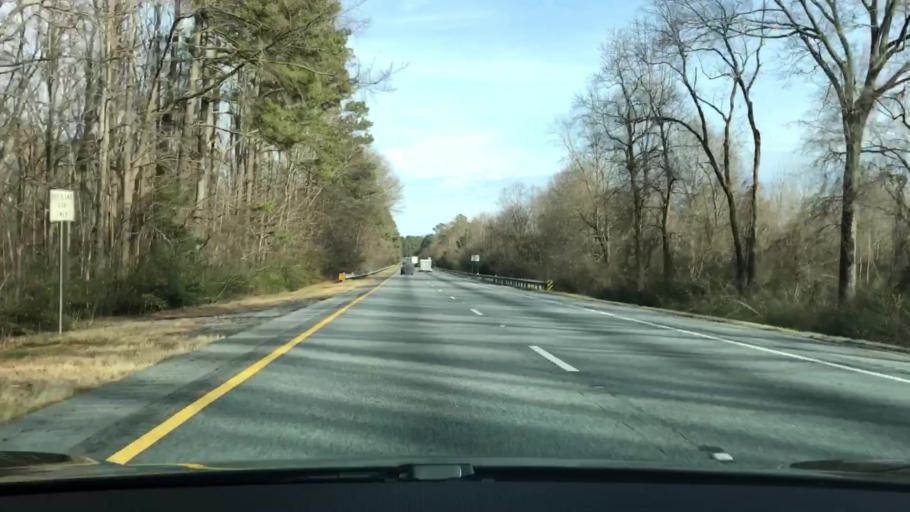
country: US
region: Georgia
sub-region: Morgan County
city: Madison
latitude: 33.5768
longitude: -83.5498
